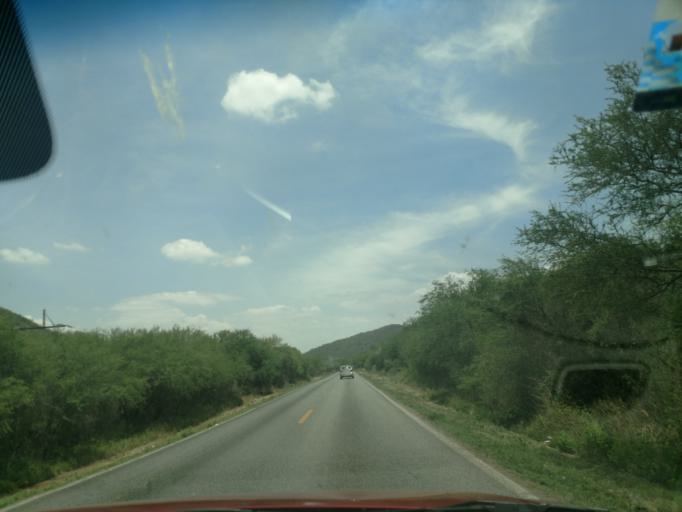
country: MX
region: San Luis Potosi
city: Ciudad Fernandez
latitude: 21.9993
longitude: -100.1413
